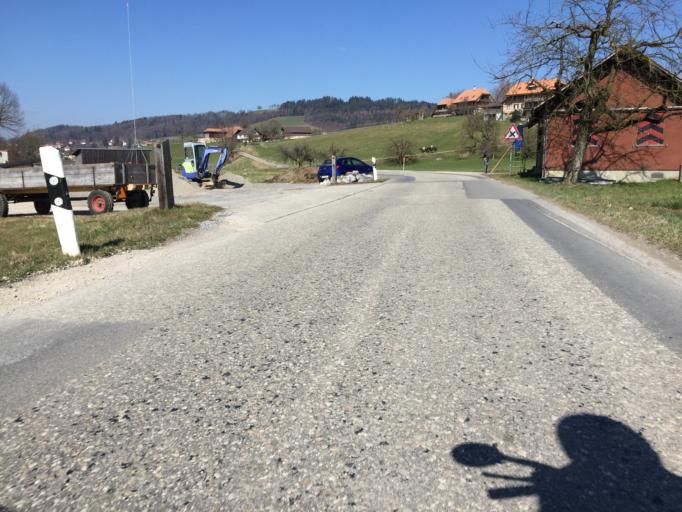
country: CH
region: Bern
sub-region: Bern-Mittelland District
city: Worb
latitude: 46.9152
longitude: 7.5758
